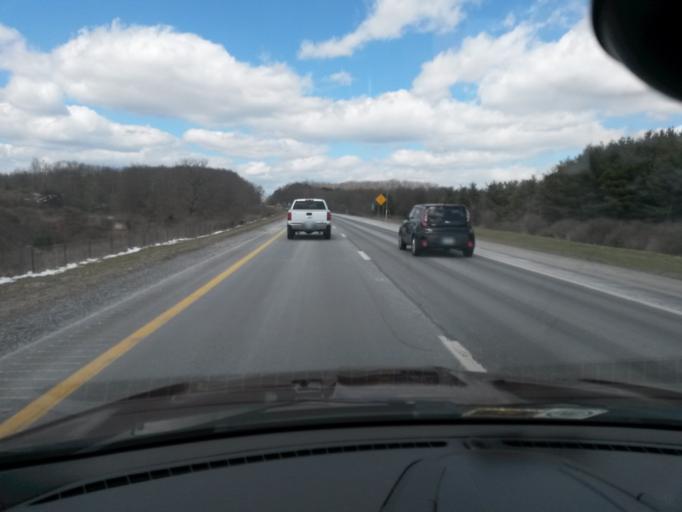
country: US
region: West Virginia
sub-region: Raleigh County
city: Shady Spring
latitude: 37.6359
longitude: -81.1100
